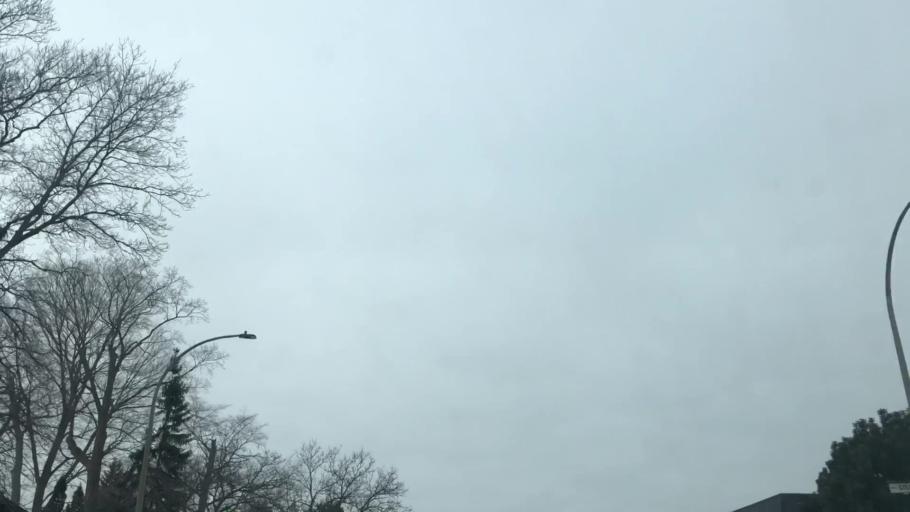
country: CA
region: Quebec
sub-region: Laval
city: Laval
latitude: 45.5226
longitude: -73.7382
